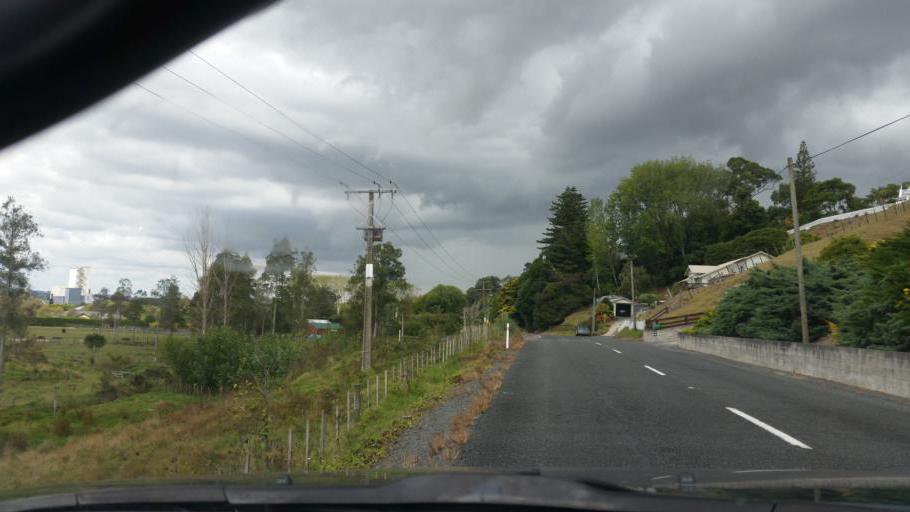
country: NZ
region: Northland
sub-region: Kaipara District
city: Dargaville
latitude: -35.9528
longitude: 173.8569
